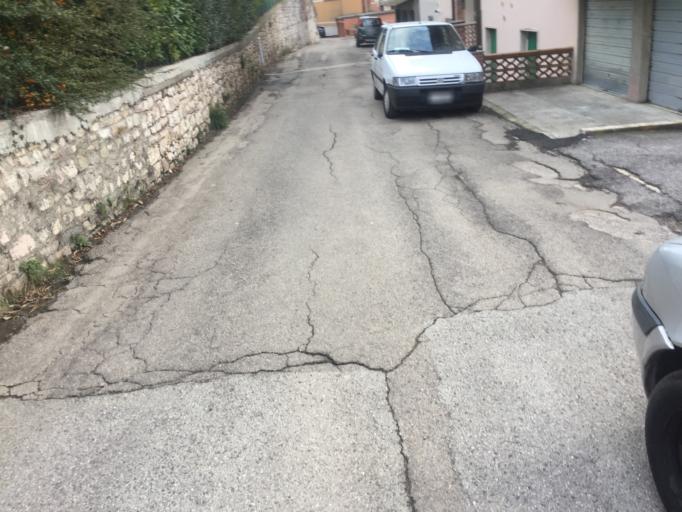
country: IT
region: Umbria
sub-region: Provincia di Perugia
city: Perugia
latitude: 43.1179
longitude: 12.4071
